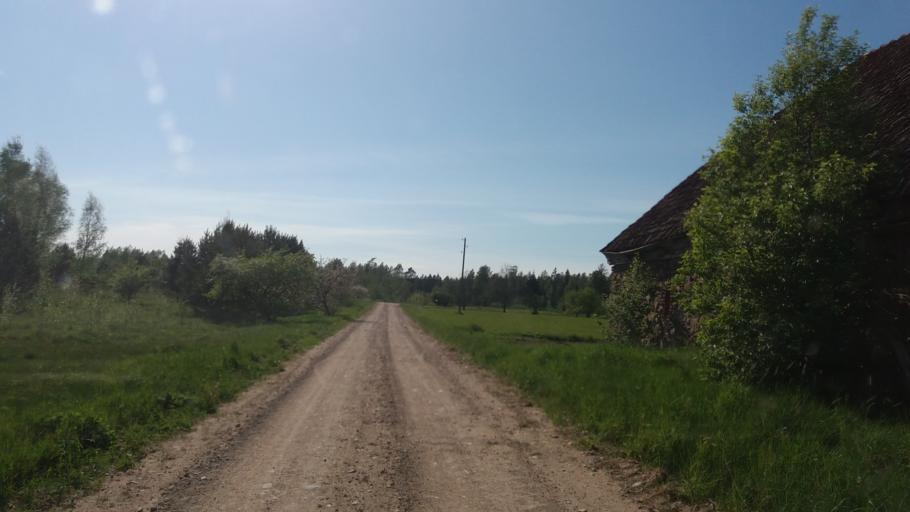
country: LV
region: Talsu Rajons
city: Stende
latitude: 57.0492
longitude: 22.2993
